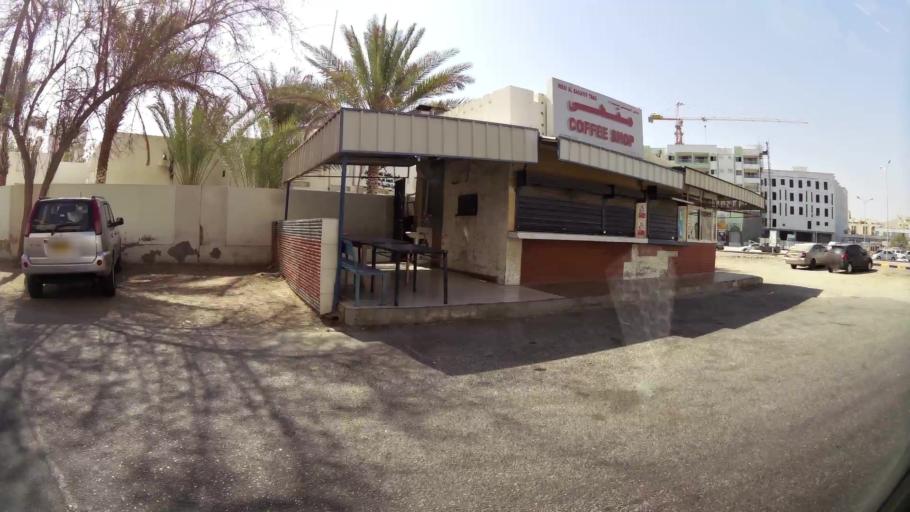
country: OM
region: Muhafazat Masqat
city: Muscat
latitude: 23.5958
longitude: 58.5462
